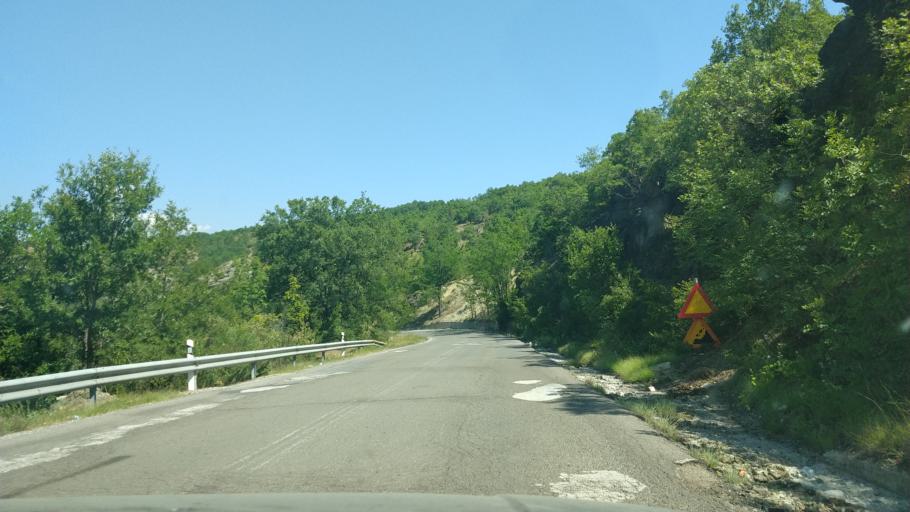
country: GR
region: West Macedonia
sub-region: Nomos Grevenon
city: Grevena
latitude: 40.0499
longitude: 21.4826
